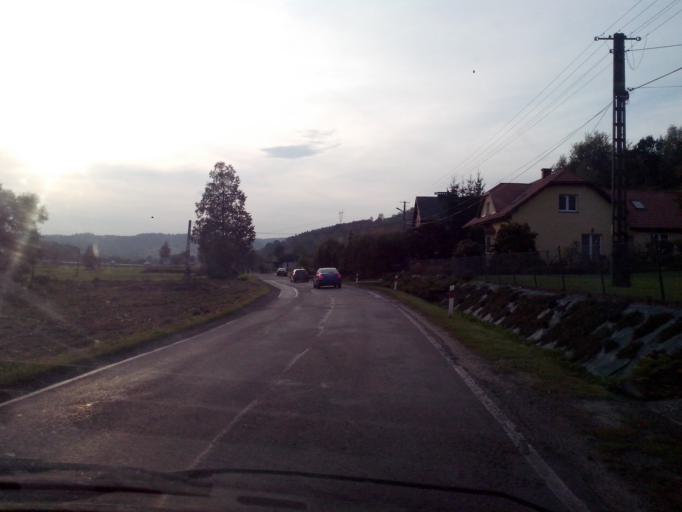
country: PL
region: Subcarpathian Voivodeship
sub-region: Powiat strzyzowski
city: Jawornik
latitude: 49.8087
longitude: 21.8783
